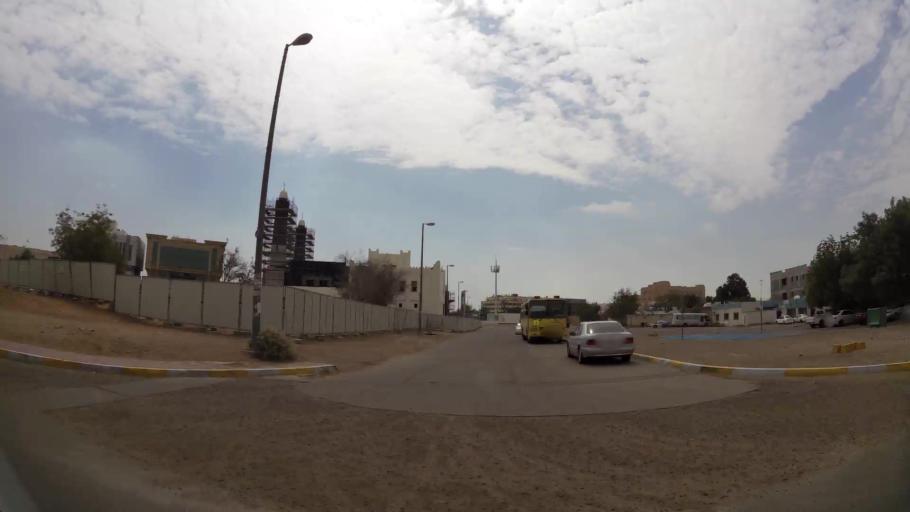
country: OM
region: Al Buraimi
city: Al Buraymi
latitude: 24.2237
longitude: 55.7784
